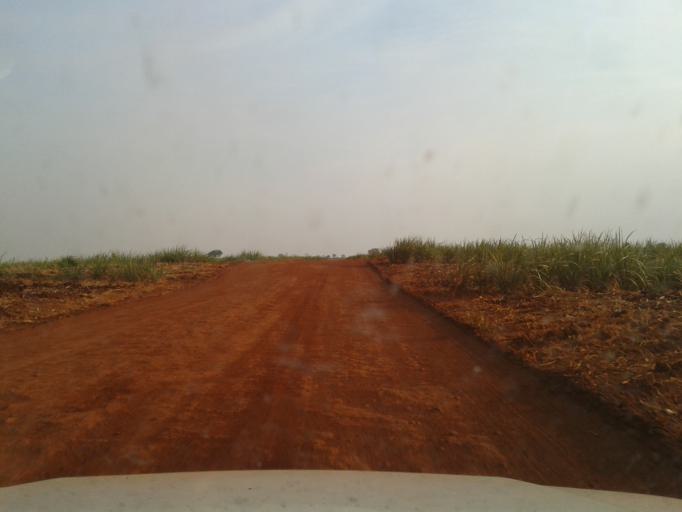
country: BR
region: Minas Gerais
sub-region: Capinopolis
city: Capinopolis
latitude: -18.7419
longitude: -49.6909
